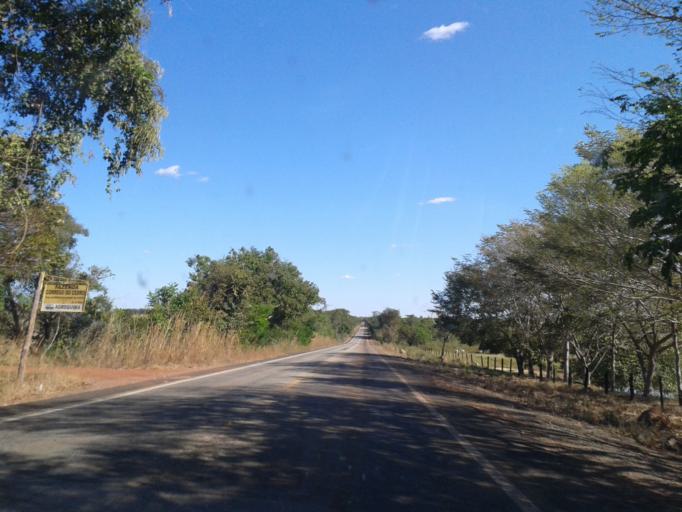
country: BR
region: Goias
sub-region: Mozarlandia
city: Mozarlandia
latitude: -14.6052
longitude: -50.5132
